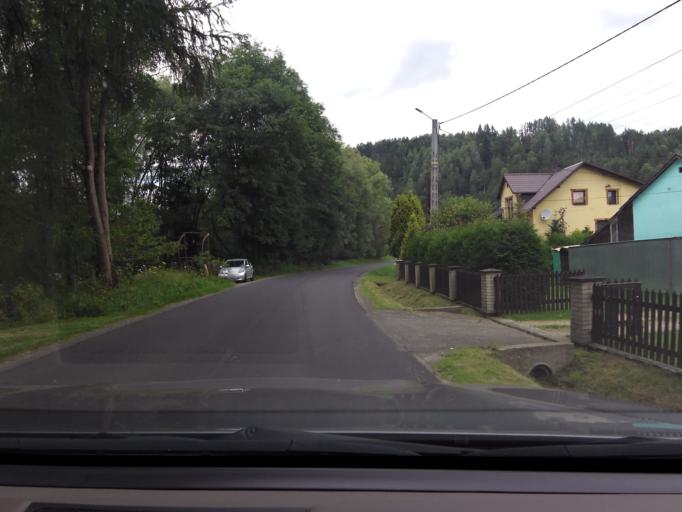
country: PL
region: Silesian Voivodeship
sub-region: Powiat zywiecki
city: Ujsoly
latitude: 49.4897
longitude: 19.1221
